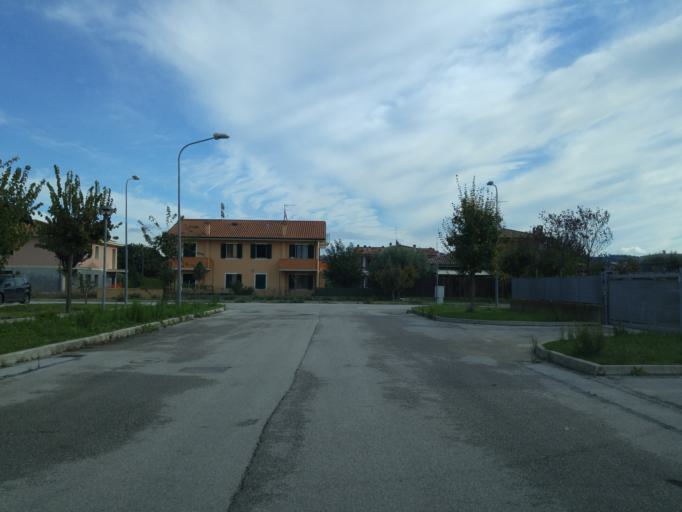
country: IT
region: The Marches
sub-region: Provincia di Pesaro e Urbino
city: Calcinelli
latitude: 43.7553
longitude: 12.9256
